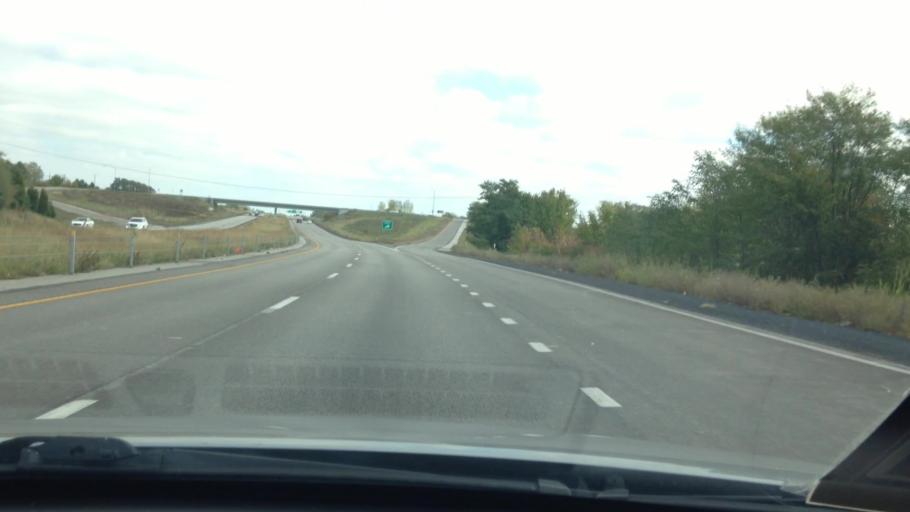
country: US
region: Missouri
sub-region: Clay County
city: Gladstone
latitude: 39.2544
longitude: -94.6065
